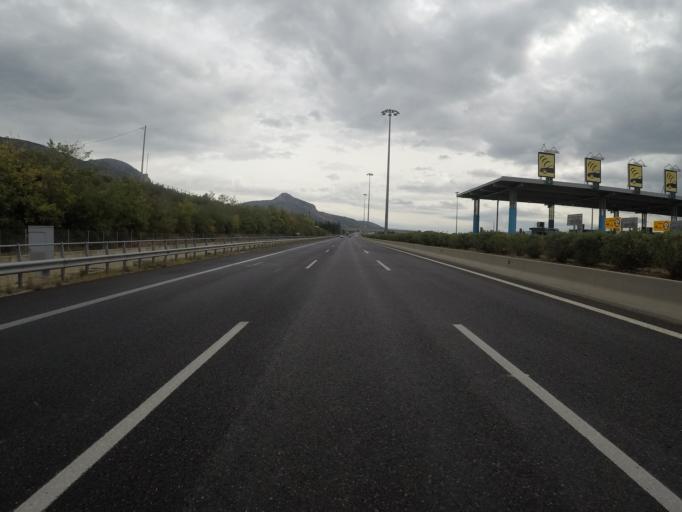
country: GR
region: Attica
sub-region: Nomarchia Dytikis Attikis
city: Aspropyrgos
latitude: 38.0944
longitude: 23.5907
